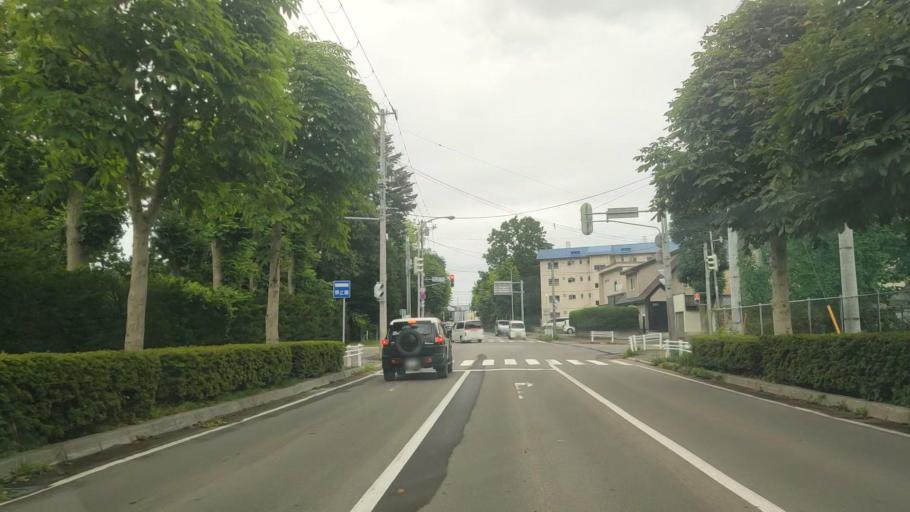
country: JP
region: Hokkaido
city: Hakodate
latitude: 41.7942
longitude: 140.7613
